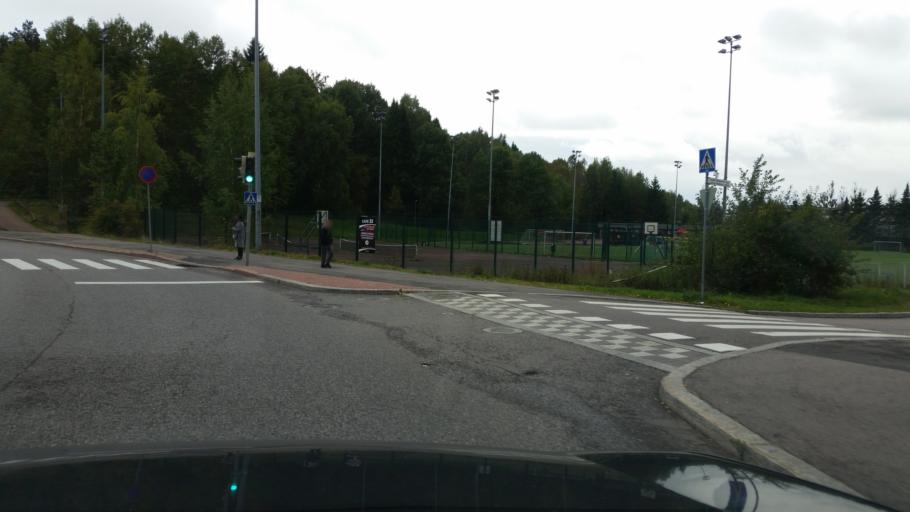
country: FI
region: Uusimaa
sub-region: Helsinki
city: Vantaa
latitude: 60.2395
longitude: 25.0023
